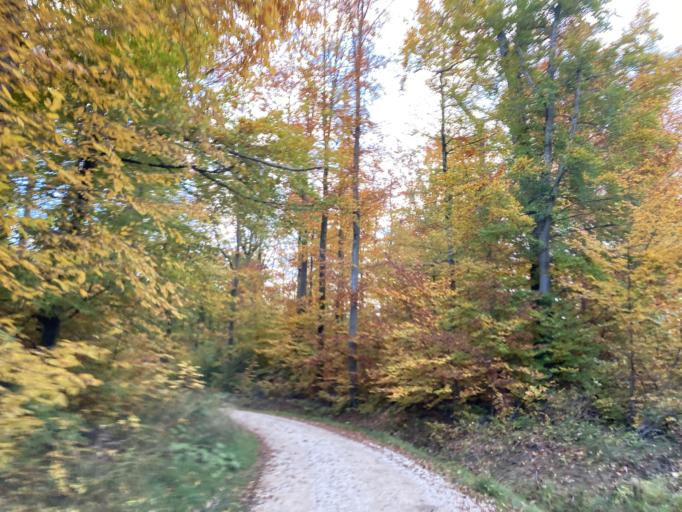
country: DE
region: Baden-Wuerttemberg
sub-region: Tuebingen Region
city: Gomaringen
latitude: 48.4623
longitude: 9.1312
